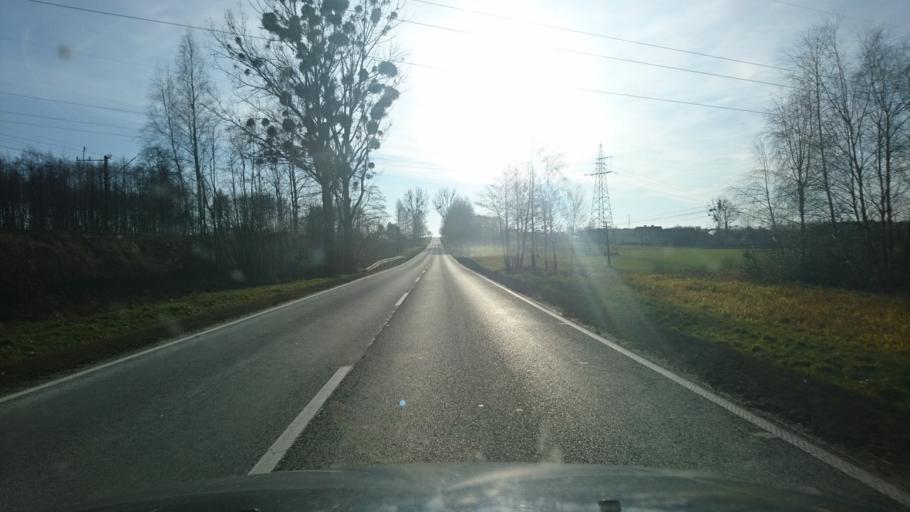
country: PL
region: Opole Voivodeship
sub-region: Powiat oleski
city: Dalachow
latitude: 51.0684
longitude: 18.6013
